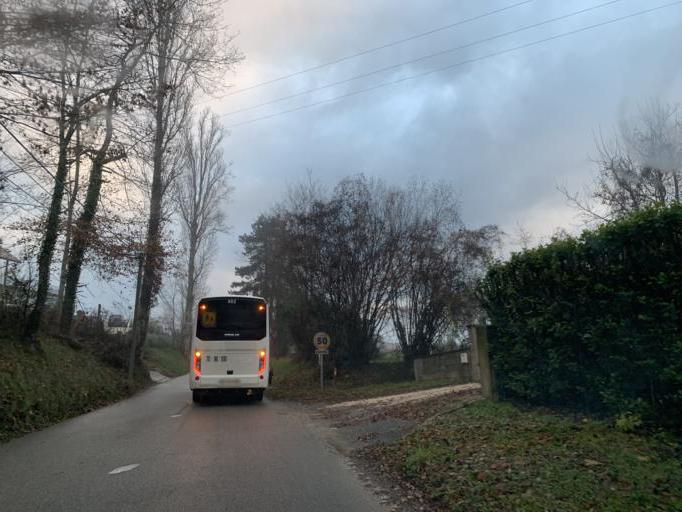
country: FR
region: Rhone-Alpes
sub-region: Departement de l'Ain
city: Belley
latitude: 45.7886
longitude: 5.6908
